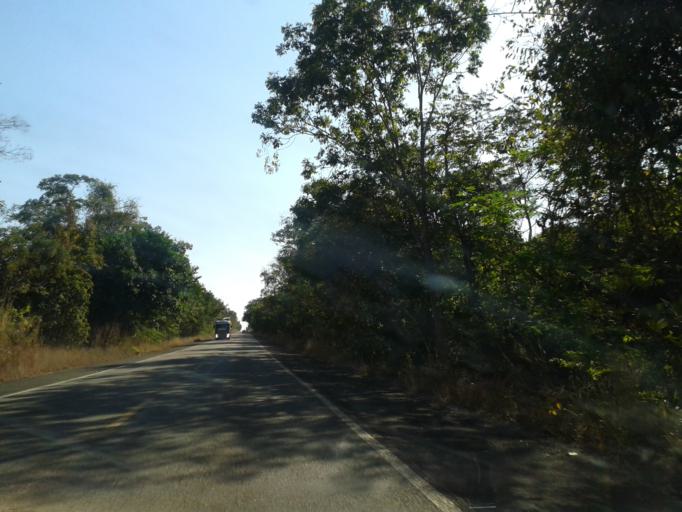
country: BR
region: Goias
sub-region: Mozarlandia
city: Mozarlandia
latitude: -15.0364
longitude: -50.6033
